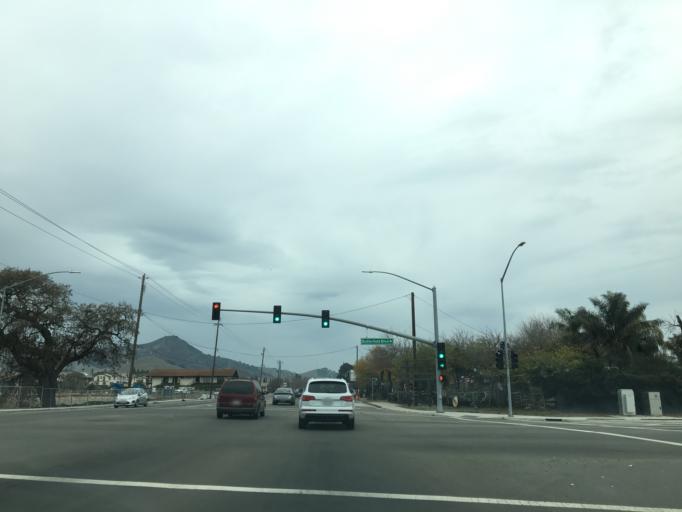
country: US
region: California
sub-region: Santa Clara County
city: Morgan Hill
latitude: 37.1076
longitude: -121.6350
